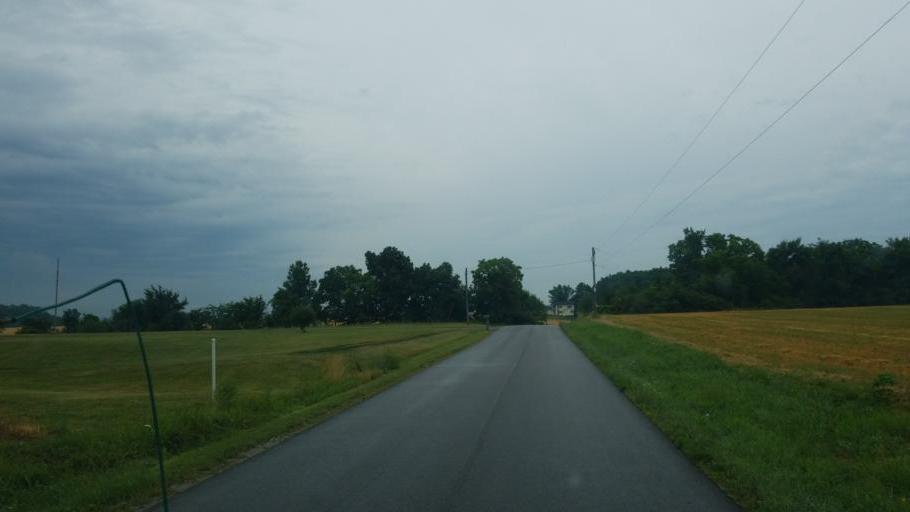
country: US
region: Ohio
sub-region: Williams County
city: Edgerton
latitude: 41.4277
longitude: -84.6701
